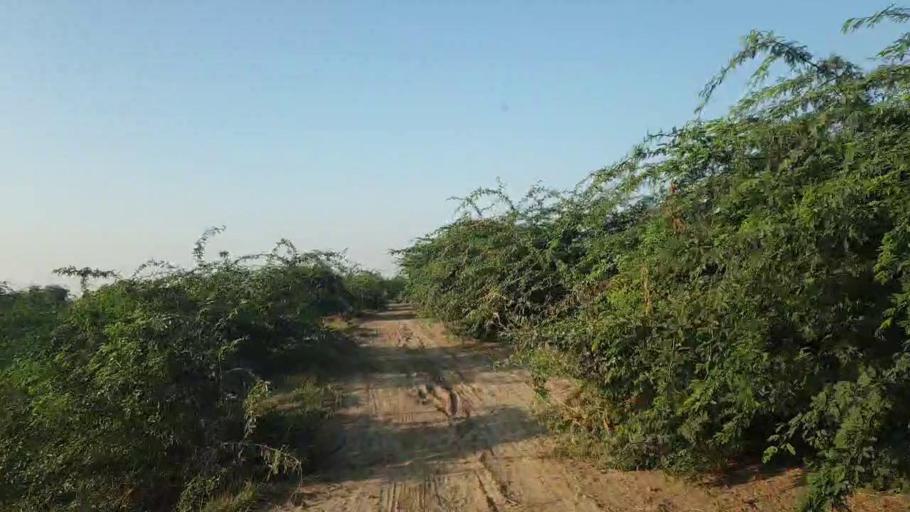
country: PK
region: Sindh
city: Badin
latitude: 24.6248
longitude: 68.7935
